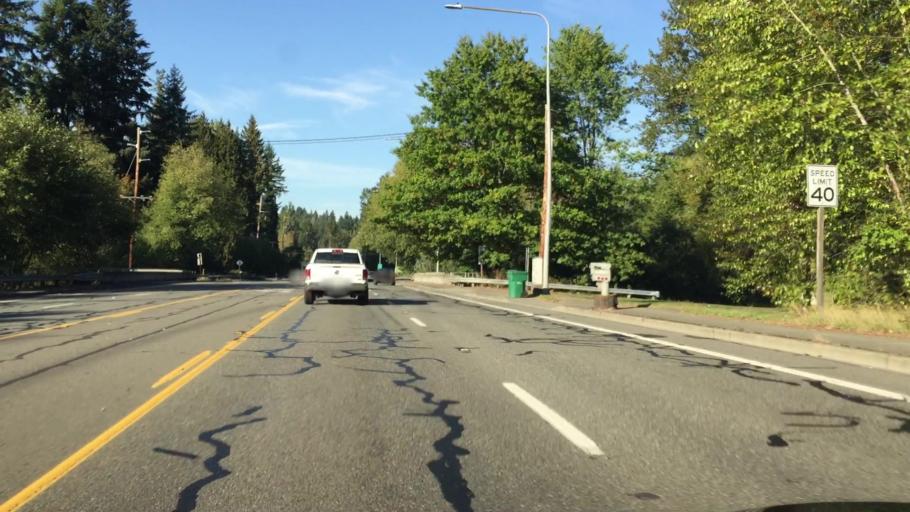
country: US
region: Washington
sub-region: King County
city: Cottage Lake
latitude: 47.7100
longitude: -122.0890
